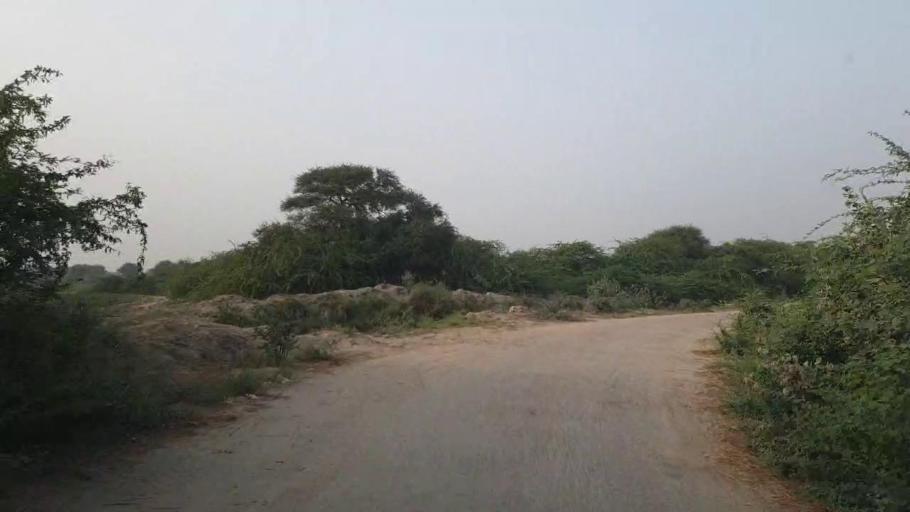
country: PK
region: Sindh
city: Mirpur Batoro
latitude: 24.6520
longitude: 68.3883
